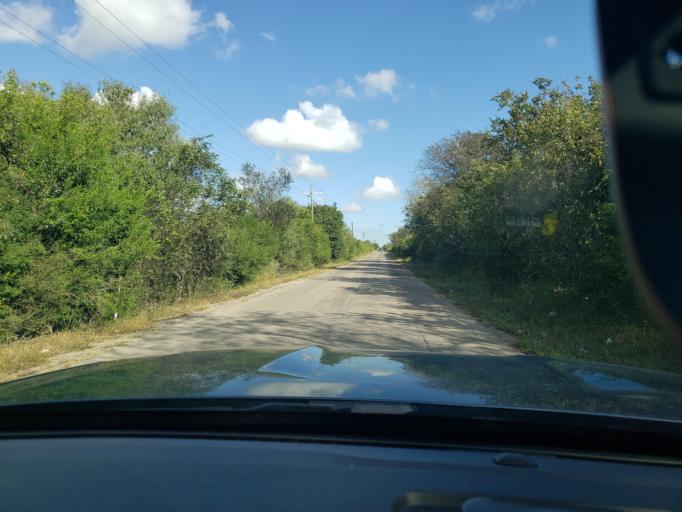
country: US
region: Texas
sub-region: Bee County
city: Beeville
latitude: 28.4547
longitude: -97.7179
